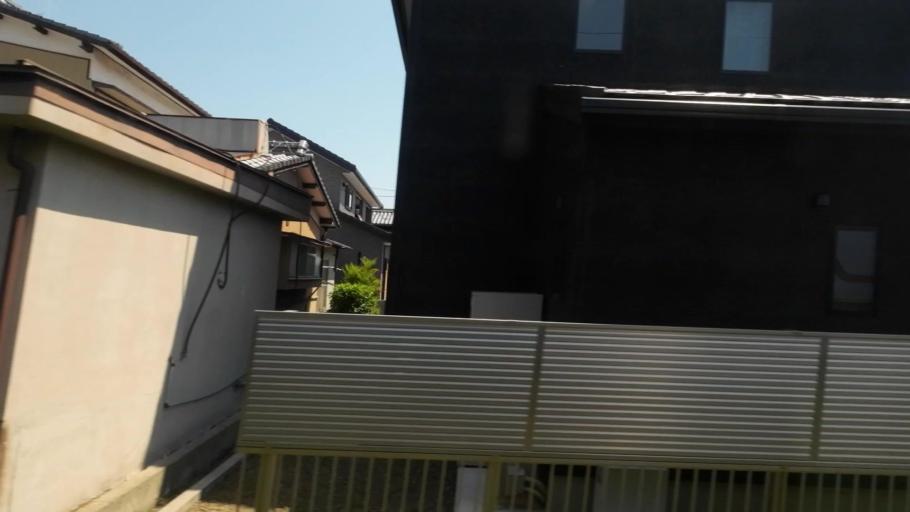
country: JP
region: Ehime
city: Saijo
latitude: 33.9338
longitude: 133.0820
